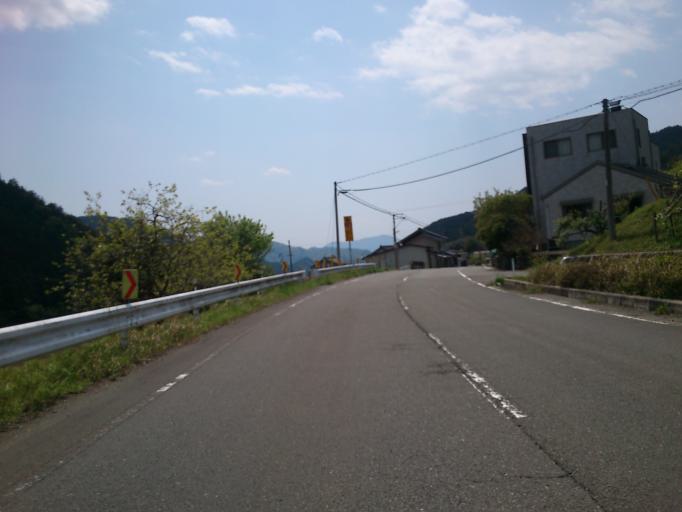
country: JP
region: Kyoto
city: Fukuchiyama
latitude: 35.3649
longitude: 134.9668
